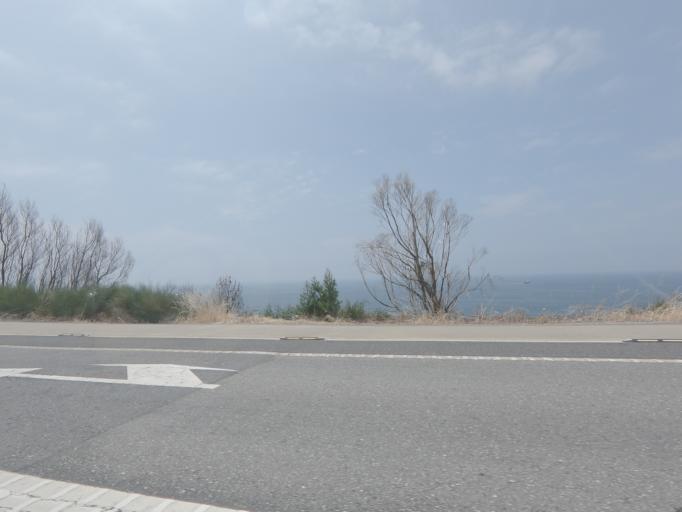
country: ES
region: Galicia
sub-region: Provincia de Pontevedra
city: A Guarda
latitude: 41.9394
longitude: -8.8844
